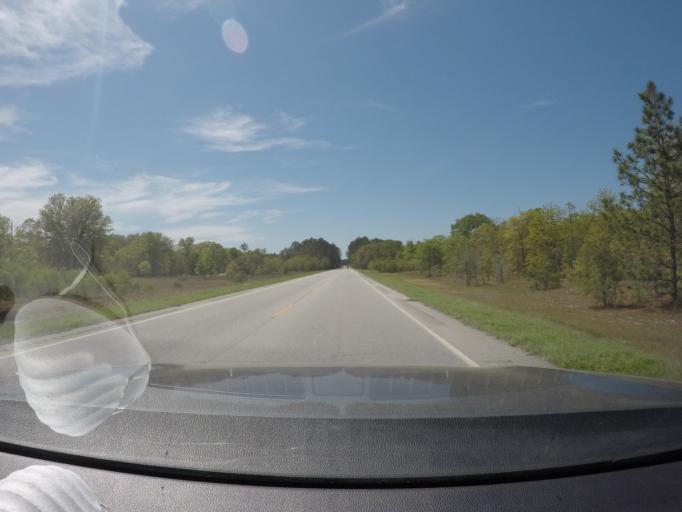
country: US
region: Georgia
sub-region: Evans County
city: Claxton
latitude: 32.1471
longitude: -81.7694
